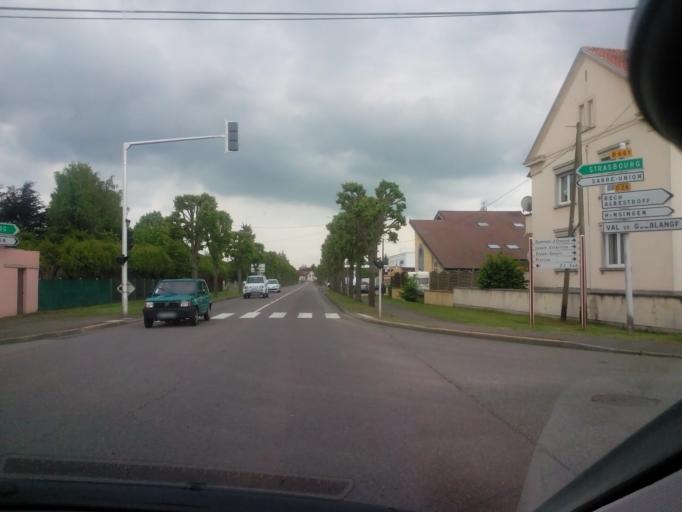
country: FR
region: Lorraine
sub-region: Departement de la Moselle
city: Sarralbe
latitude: 48.9961
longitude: 7.0248
